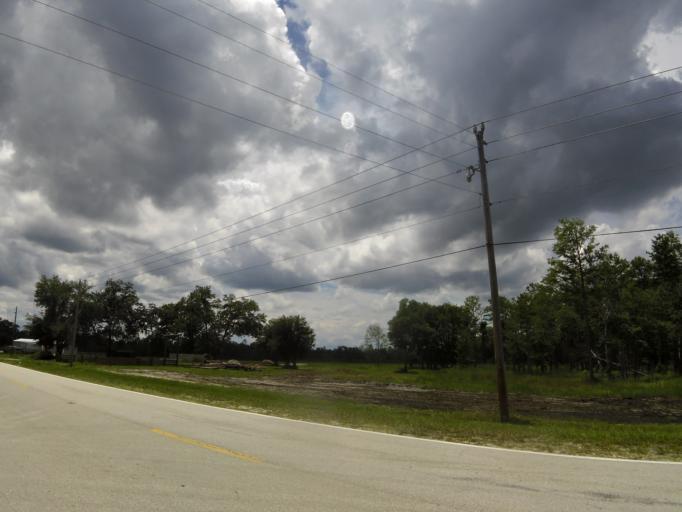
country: US
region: Florida
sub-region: Flagler County
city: Bunnell
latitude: 29.4239
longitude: -81.2261
